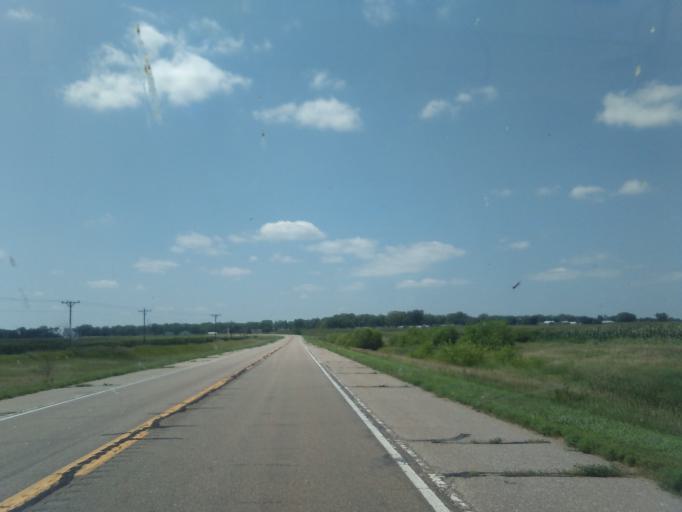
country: US
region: Nebraska
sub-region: Gosper County
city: Elwood
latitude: 40.6846
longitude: -99.8155
